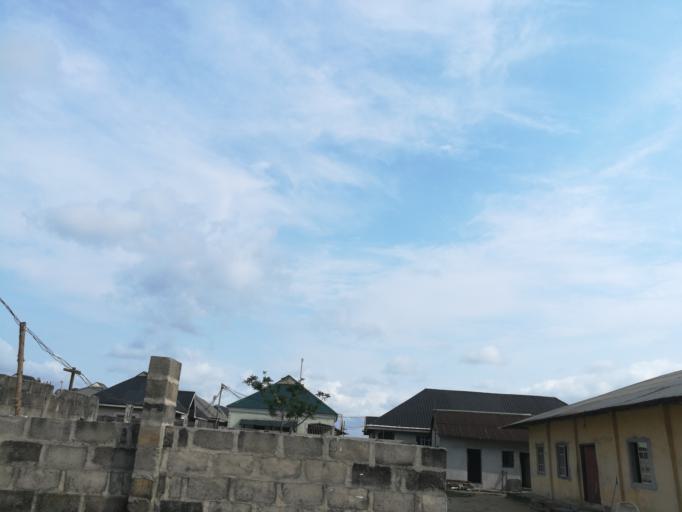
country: NG
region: Rivers
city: Okrika
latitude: 4.7467
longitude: 7.0863
